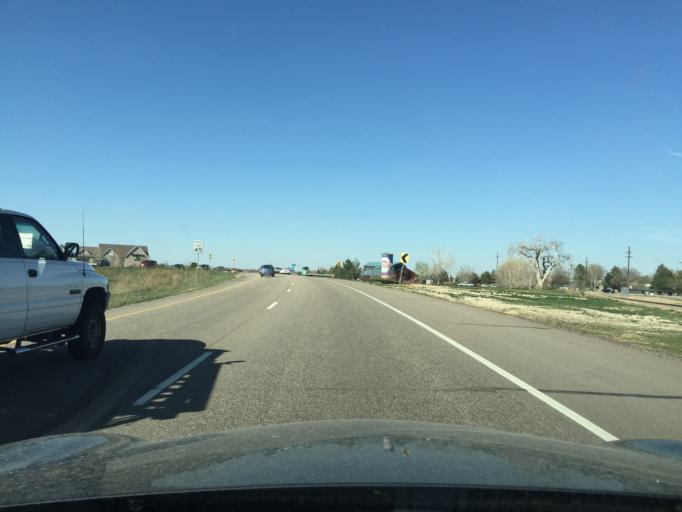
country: US
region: Colorado
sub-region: Boulder County
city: Longmont
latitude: 40.1372
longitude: -105.1332
